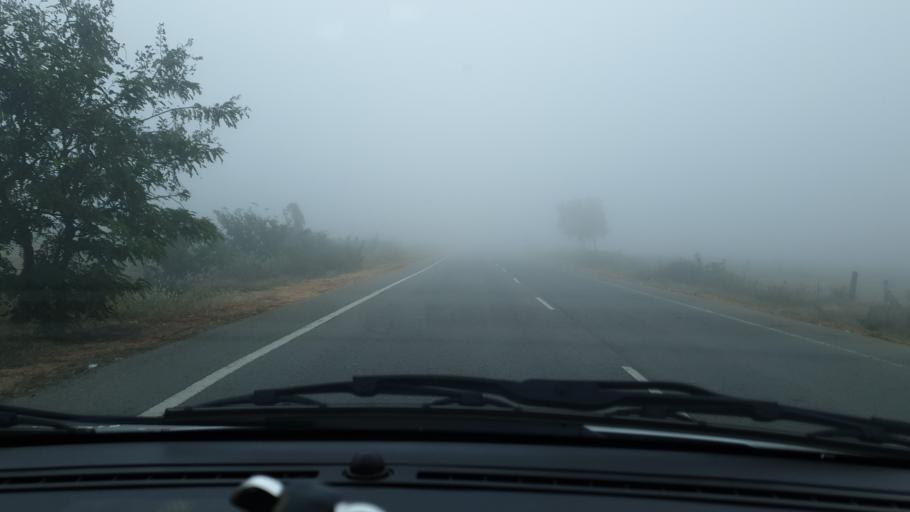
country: IN
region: Telangana
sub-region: Mahbubnagar
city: Nagar Karnul
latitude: 16.6749
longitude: 78.5300
